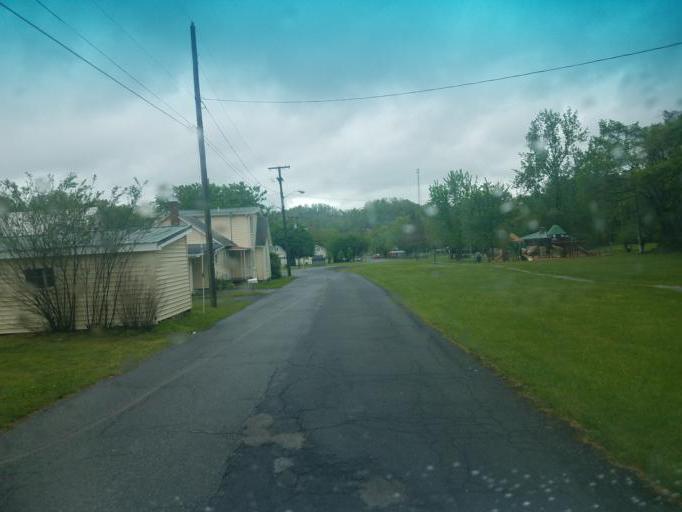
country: US
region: Virginia
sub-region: Washington County
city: Emory
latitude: 36.6327
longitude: -81.7917
